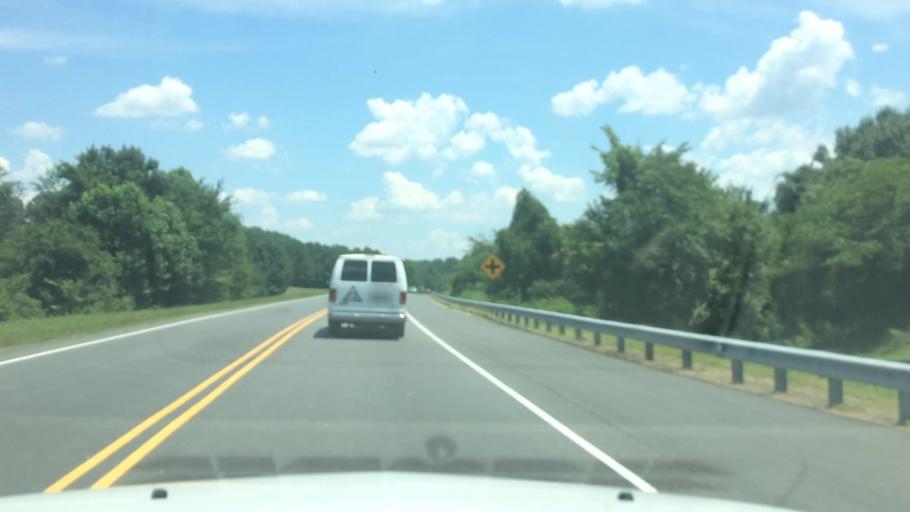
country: US
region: North Carolina
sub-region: Alexander County
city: Stony Point
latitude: 35.8153
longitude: -80.9864
